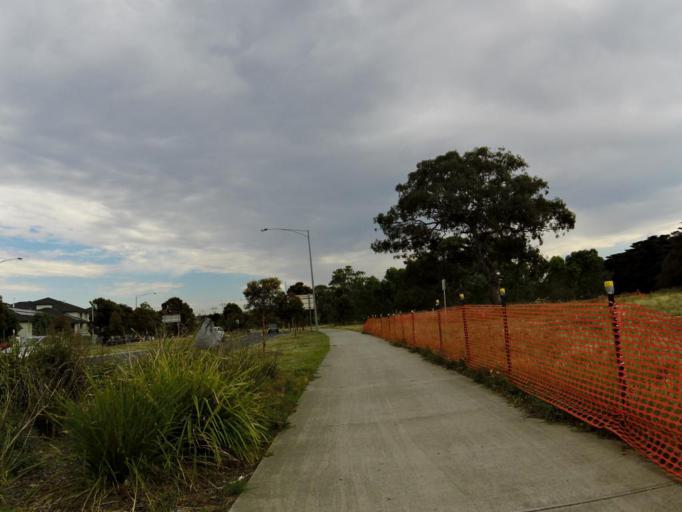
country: AU
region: Victoria
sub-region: Whittlesea
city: Mill Park
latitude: -37.6483
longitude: 145.0663
